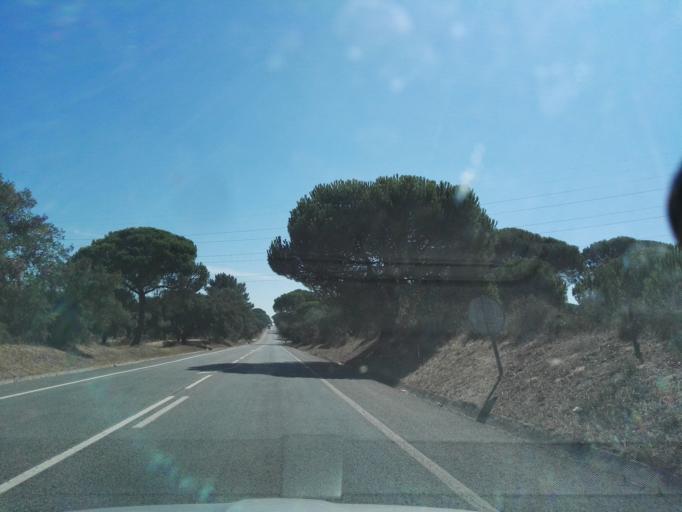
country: PT
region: Santarem
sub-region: Benavente
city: Samora Correia
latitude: 38.8960
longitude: -8.8372
